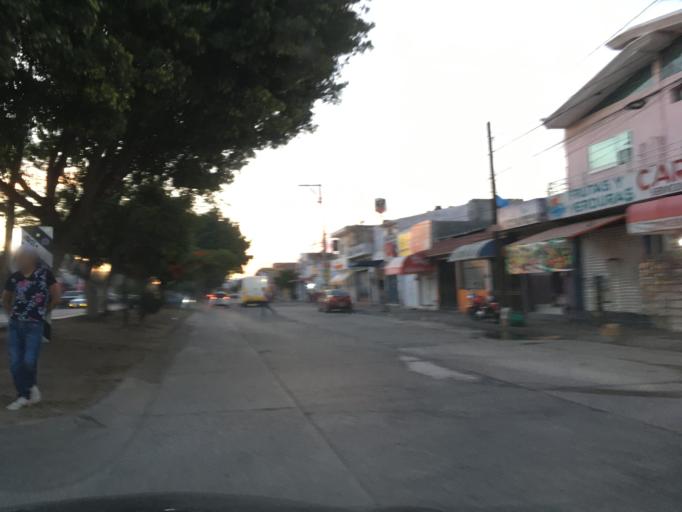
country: MX
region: Guanajuato
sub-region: Leon
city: San Jose de Duran (Los Troncoso)
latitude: 21.0798
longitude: -101.6392
